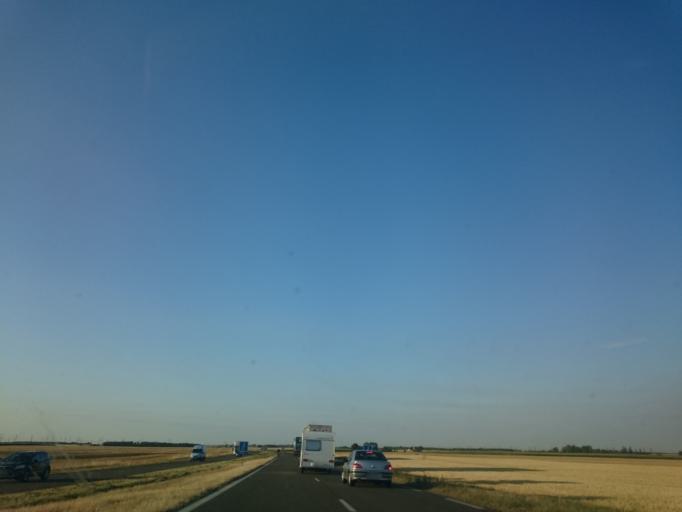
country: FR
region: Ile-de-France
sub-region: Departement de l'Essonne
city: Angerville
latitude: 48.2679
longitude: 1.9726
